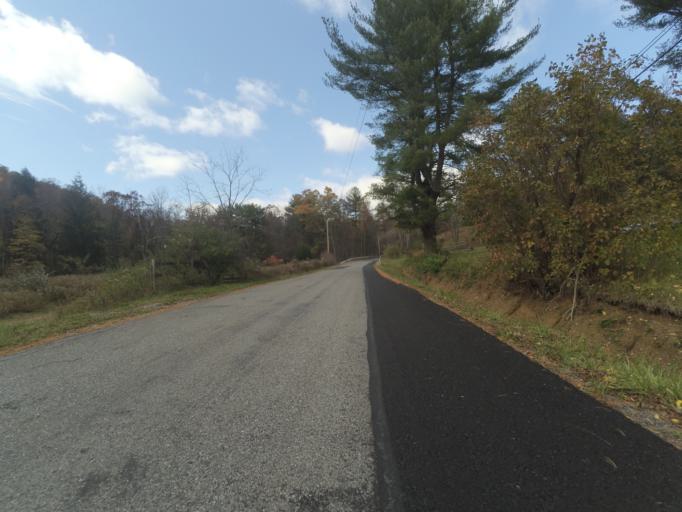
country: US
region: Pennsylvania
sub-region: Centre County
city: Stormstown
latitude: 40.8555
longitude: -77.9800
